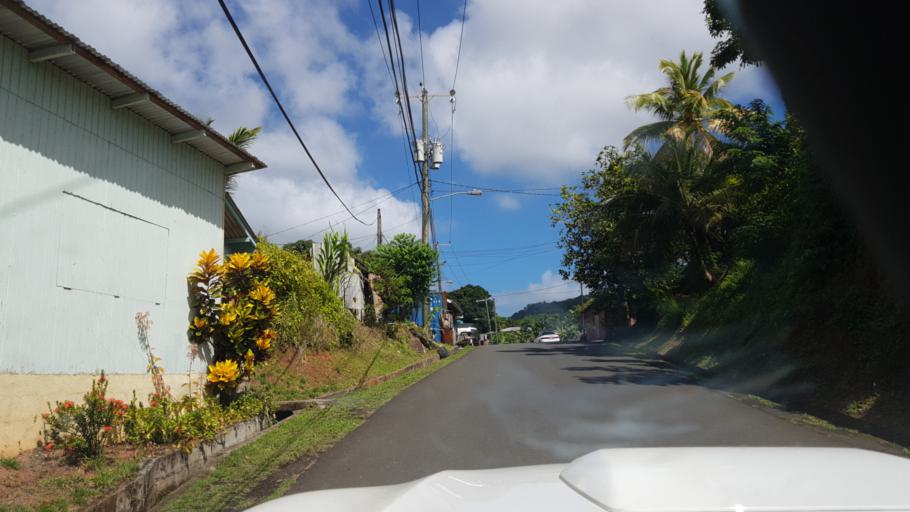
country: LC
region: Anse-la-Raye
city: Anse La Raye
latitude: 13.9401
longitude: -60.9821
